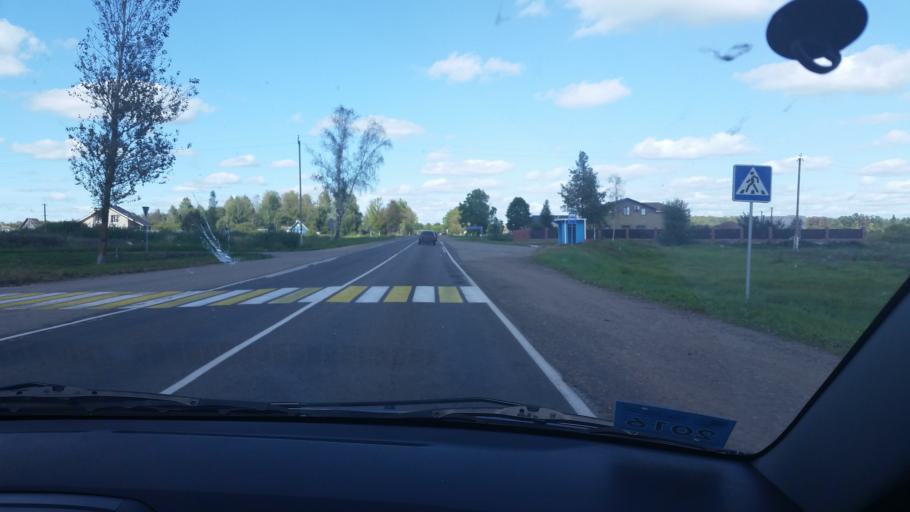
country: BY
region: Vitebsk
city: Vitebsk
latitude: 55.1118
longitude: 30.2828
